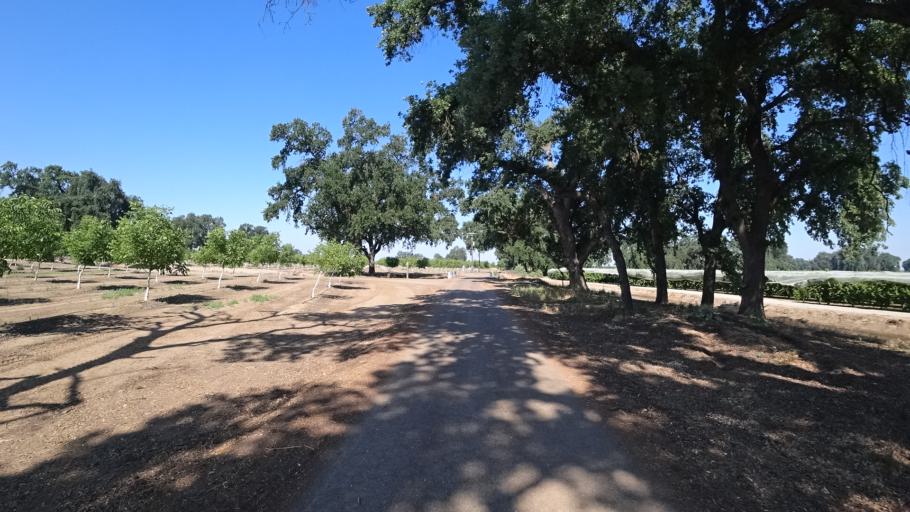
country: US
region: California
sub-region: Fresno County
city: Kingsburg
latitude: 36.4421
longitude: -119.5682
